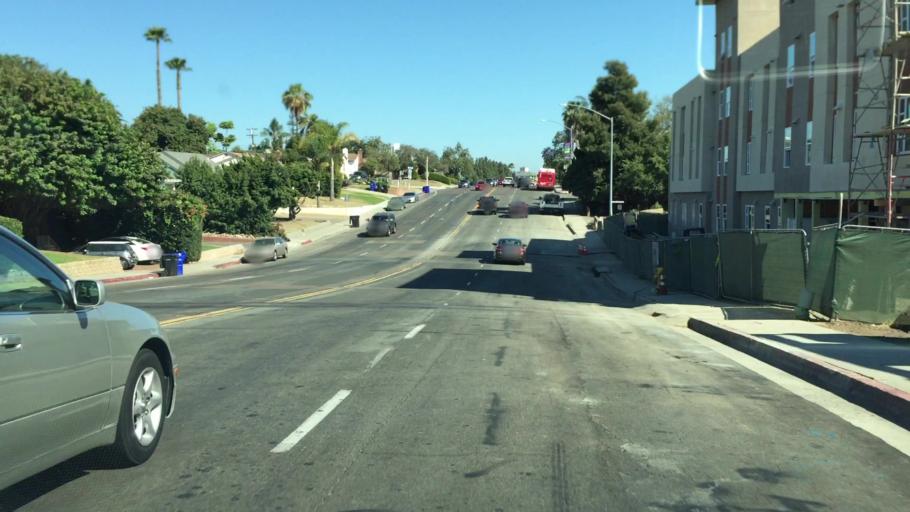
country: US
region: California
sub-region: San Diego County
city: La Mesa
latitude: 32.7696
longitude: -117.0694
